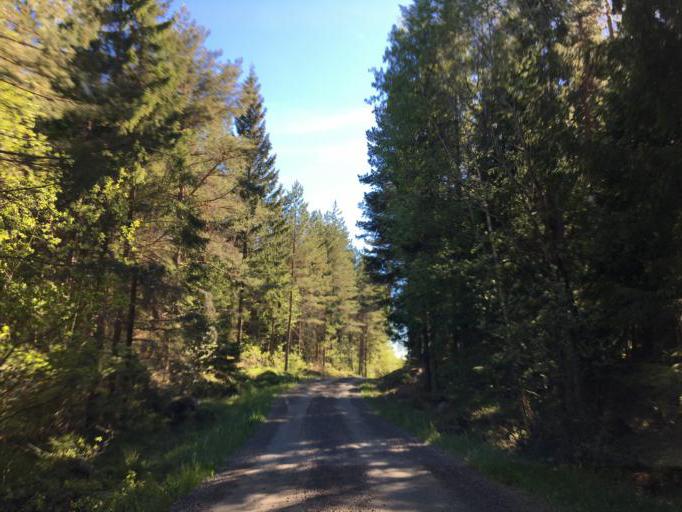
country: SE
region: Soedermanland
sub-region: Eskilstuna Kommun
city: Kvicksund
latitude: 59.3479
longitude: 16.3109
